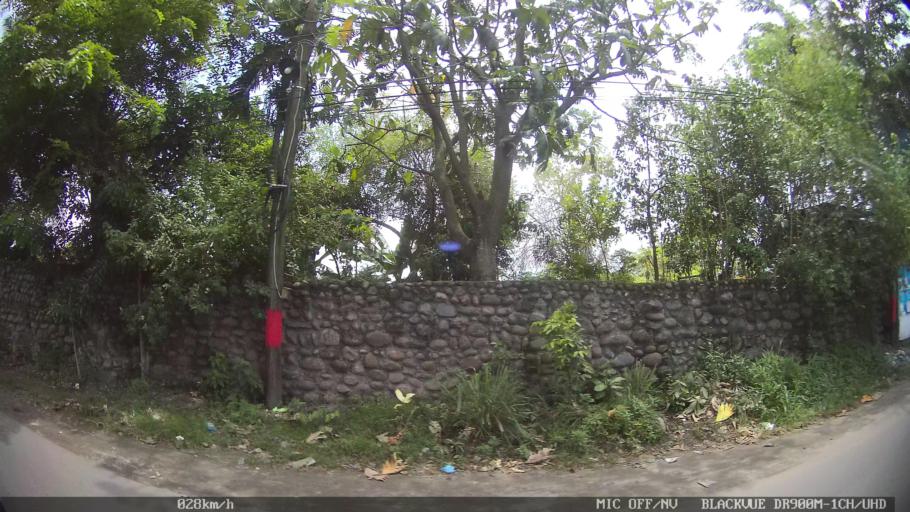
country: ID
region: North Sumatra
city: Labuhan Deli
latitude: 3.7079
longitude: 98.6782
